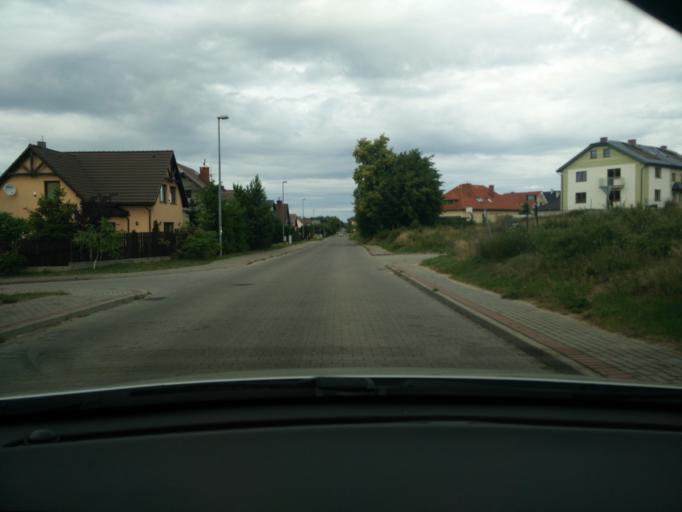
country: PL
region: Pomeranian Voivodeship
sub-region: Powiat pucki
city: Mosty
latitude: 54.6049
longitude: 18.4880
